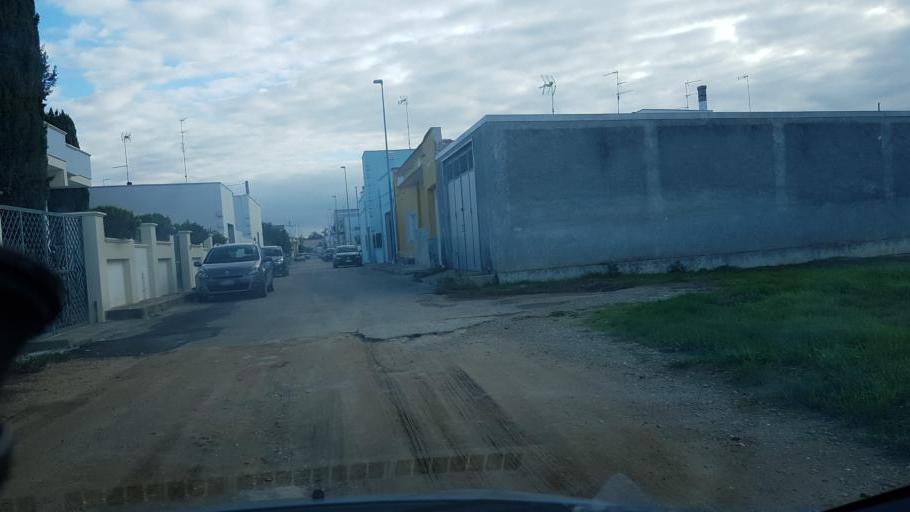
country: IT
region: Apulia
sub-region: Provincia di Lecce
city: Veglie
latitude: 40.3421
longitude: 17.9709
